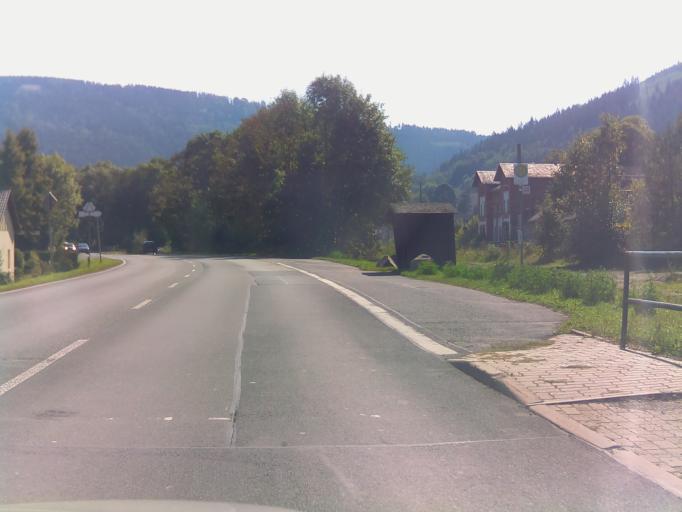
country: DE
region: Thuringia
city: Kaulsdorf
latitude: 50.6131
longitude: 11.4326
